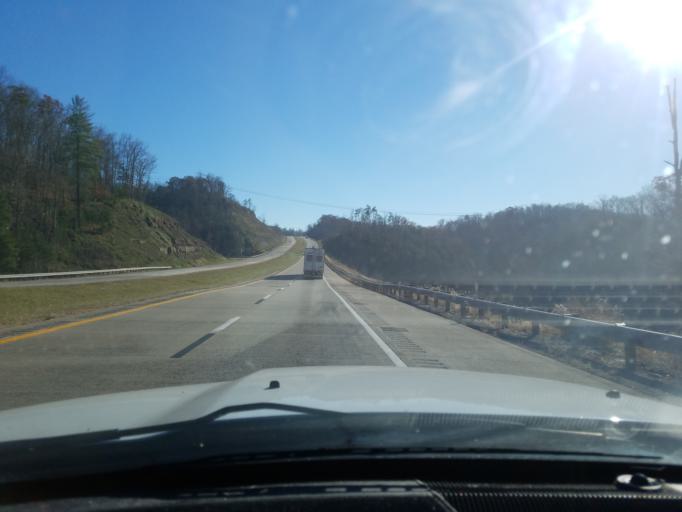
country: US
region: West Virginia
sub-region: Putnam County
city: Eleanor
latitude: 38.5145
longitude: -81.9325
